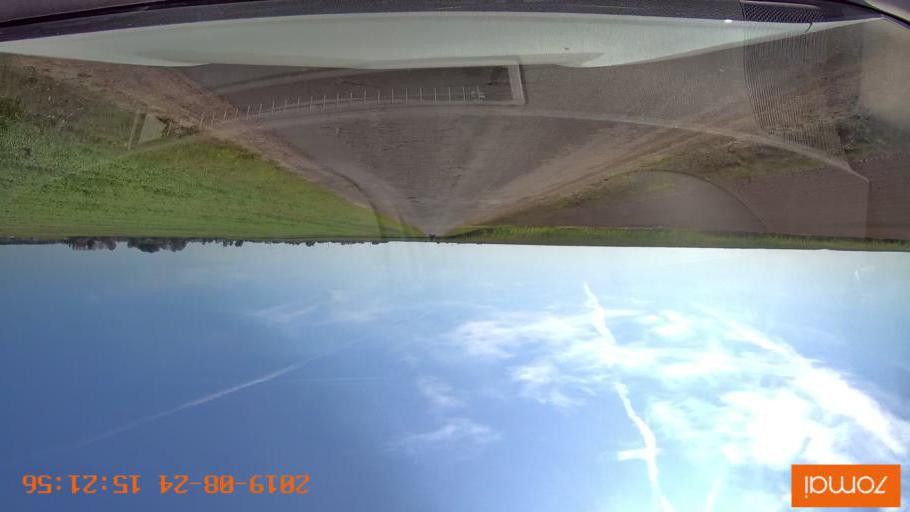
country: BY
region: Minsk
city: Samakhvalavichy
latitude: 53.6770
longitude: 27.5097
